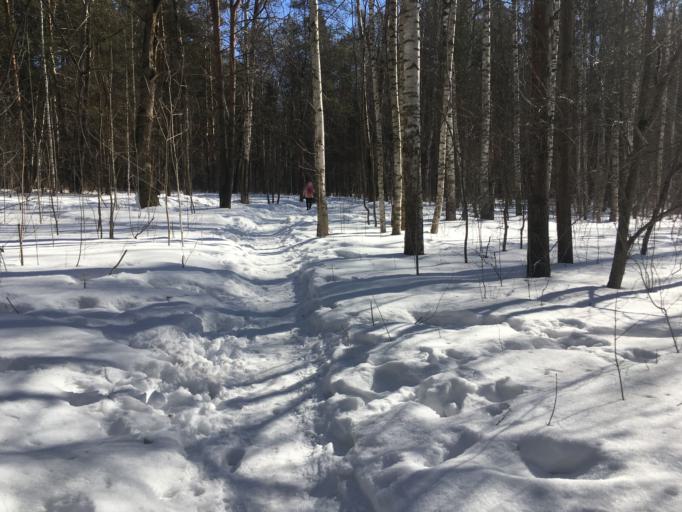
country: RU
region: Perm
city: Kondratovo
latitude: 57.9929
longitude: 56.1619
